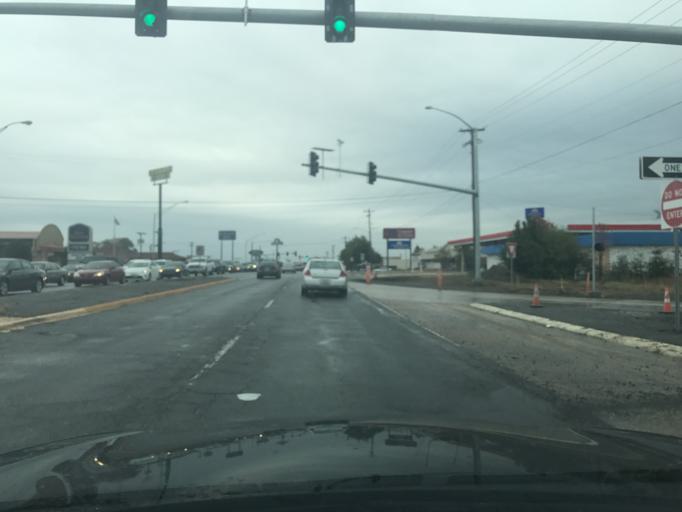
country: US
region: Arkansas
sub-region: Faulkner County
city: Conway
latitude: 35.0915
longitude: -92.4212
